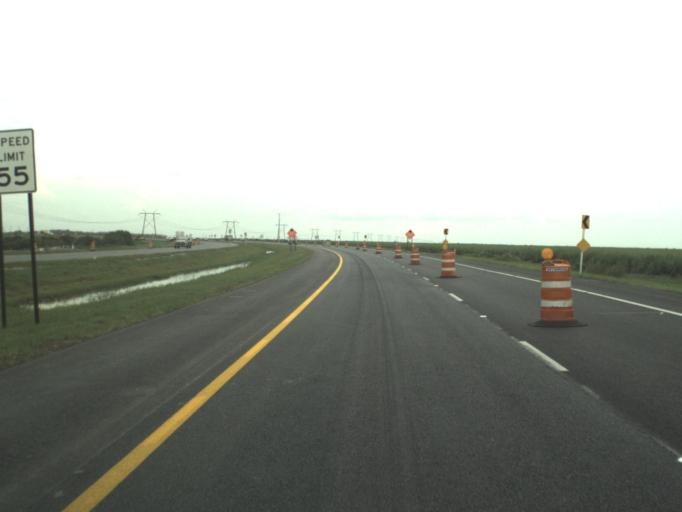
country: US
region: Florida
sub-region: Palm Beach County
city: Loxahatchee Groves
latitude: 26.7228
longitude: -80.4360
